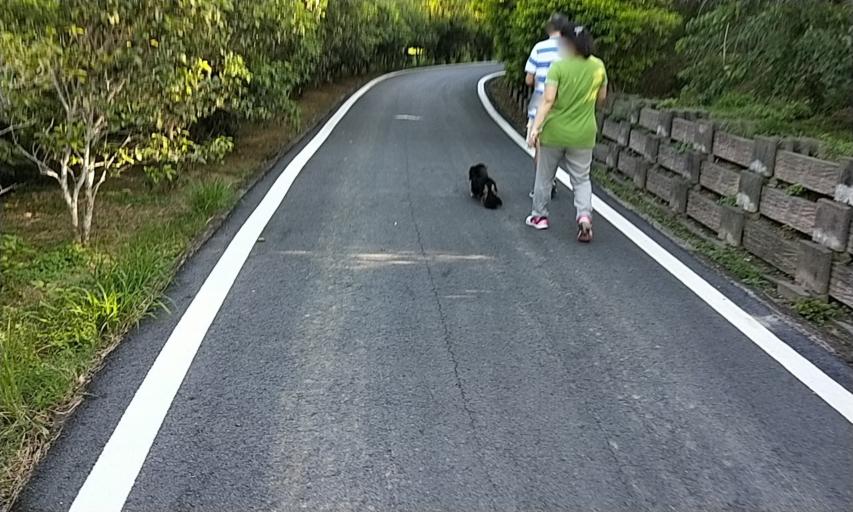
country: TW
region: Taiwan
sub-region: Hsinchu
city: Hsinchu
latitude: 24.7710
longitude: 120.9296
